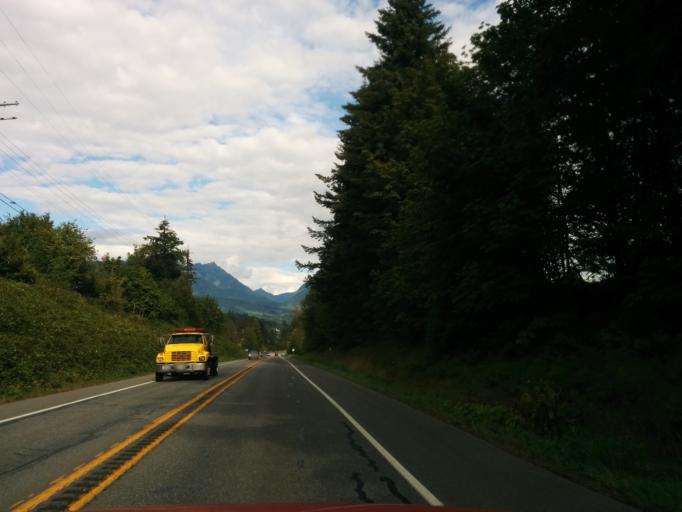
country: US
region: Washington
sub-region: Snohomish County
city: Sultan
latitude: 47.8688
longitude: -121.7715
